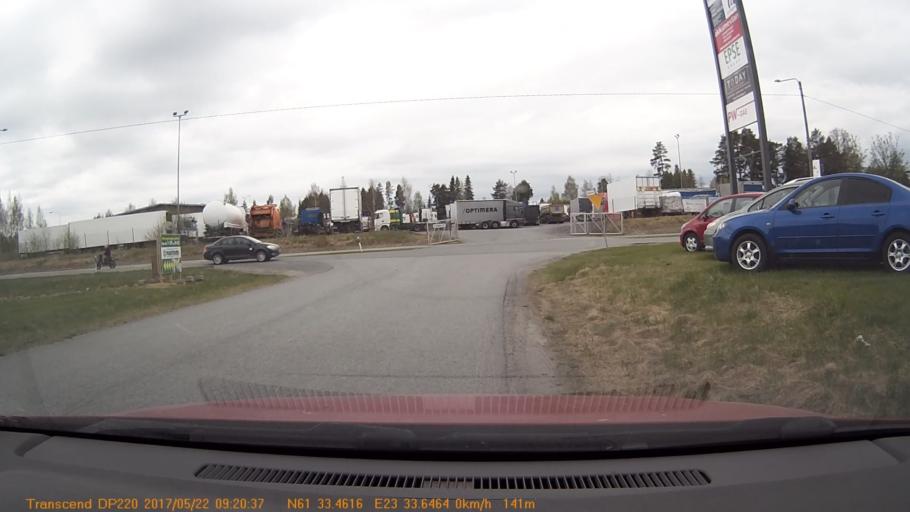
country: FI
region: Pirkanmaa
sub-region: Tampere
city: Yloejaervi
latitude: 61.5575
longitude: 23.5606
